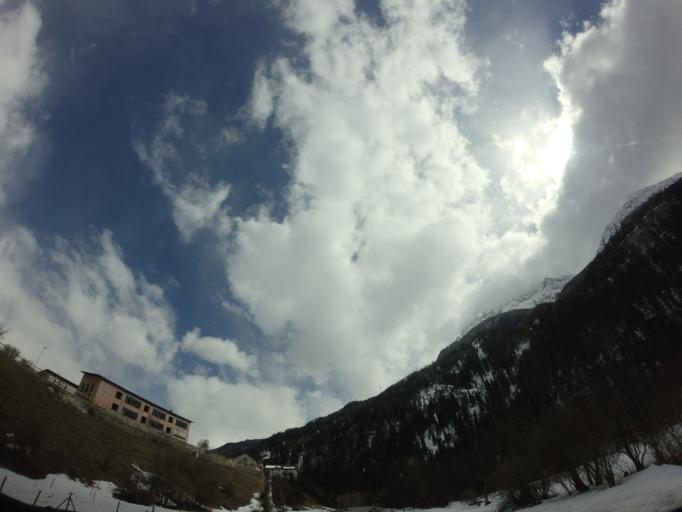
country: AT
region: Tyrol
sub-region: Politischer Bezirk Landeck
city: Nauders
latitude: 46.8618
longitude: 10.4316
